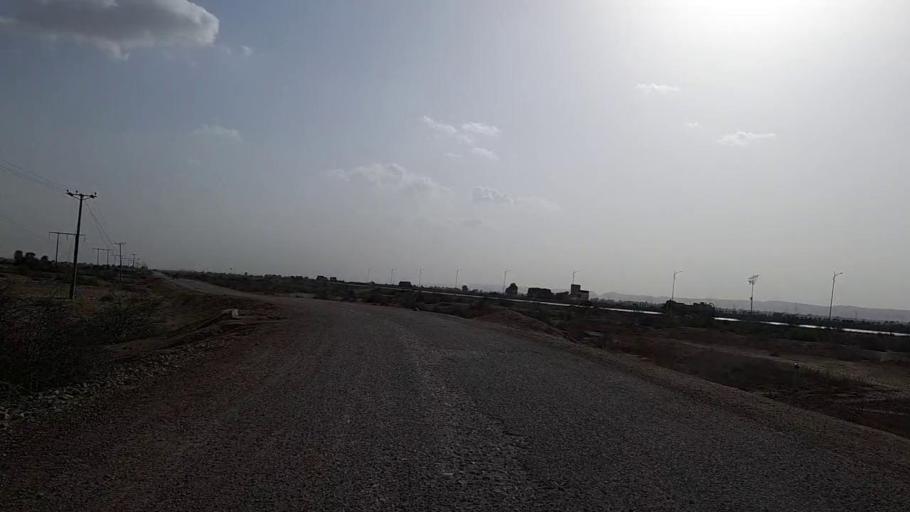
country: PK
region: Sindh
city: Kotri
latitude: 25.2452
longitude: 67.9513
